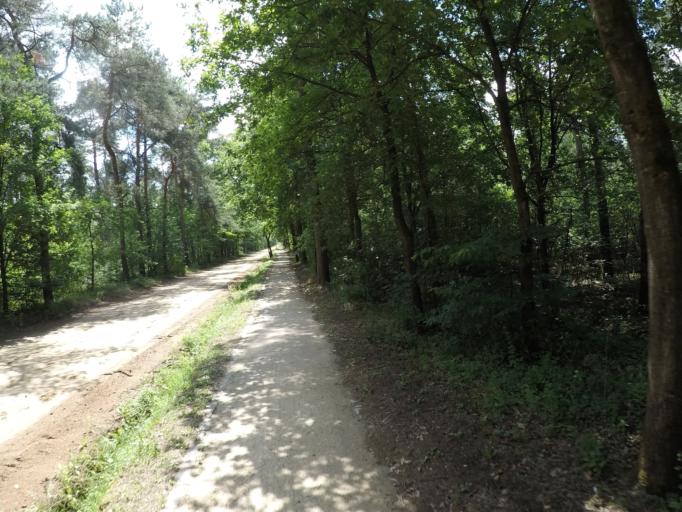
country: BE
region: Flanders
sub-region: Provincie Antwerpen
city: Beerse
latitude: 51.2891
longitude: 4.8363
